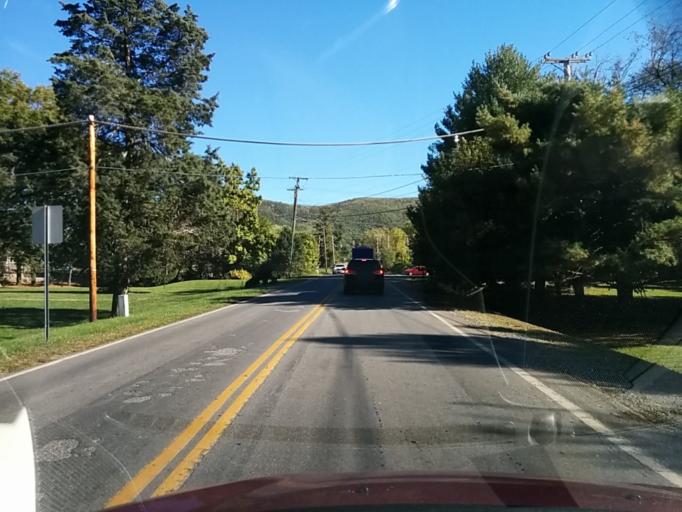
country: US
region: Virginia
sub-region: Roanoke County
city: Hollins
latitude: 37.3500
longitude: -79.9227
